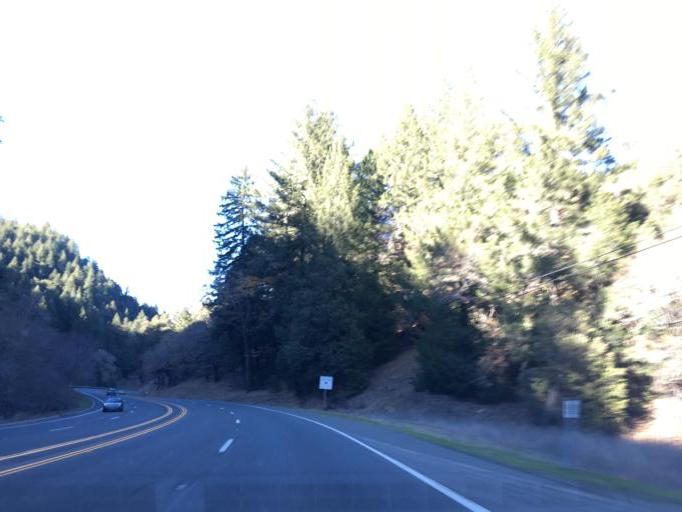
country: US
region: California
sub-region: Mendocino County
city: Laytonville
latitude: 39.5703
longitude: -123.4359
